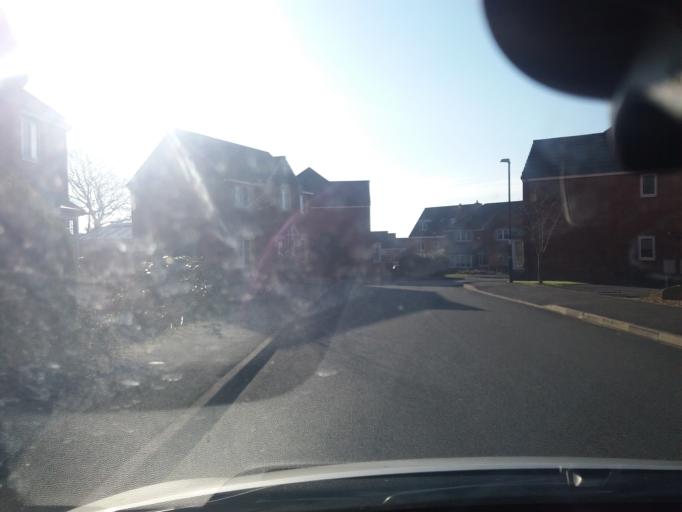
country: GB
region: England
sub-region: Lancashire
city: Adlington
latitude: 53.6210
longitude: -2.6043
